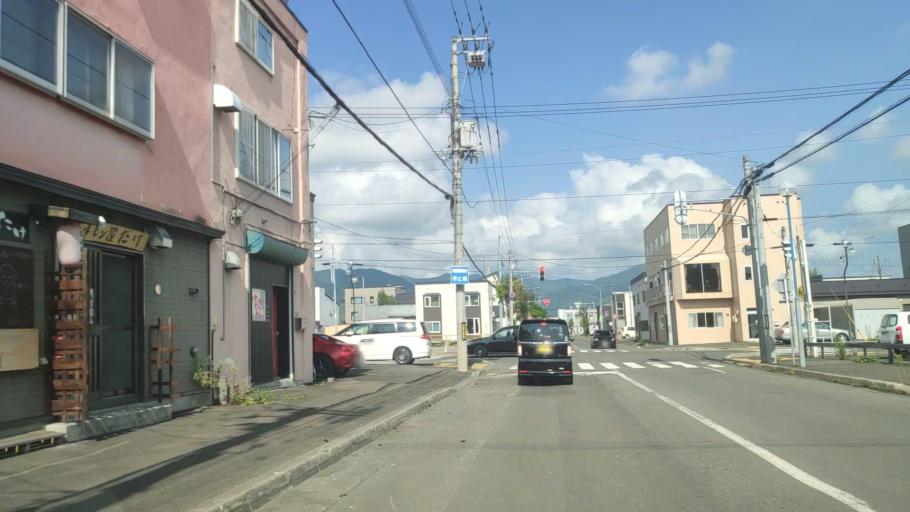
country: JP
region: Hokkaido
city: Shimo-furano
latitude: 43.3463
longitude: 142.3875
